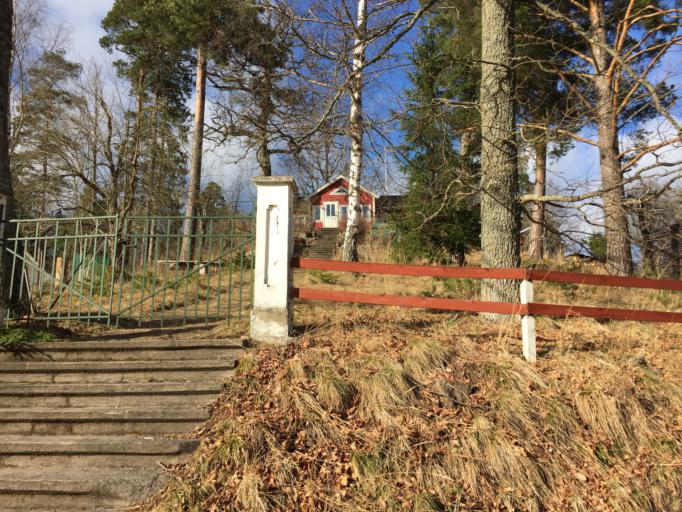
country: SE
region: Stockholm
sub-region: Salems Kommun
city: Ronninge
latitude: 59.1821
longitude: 17.7185
